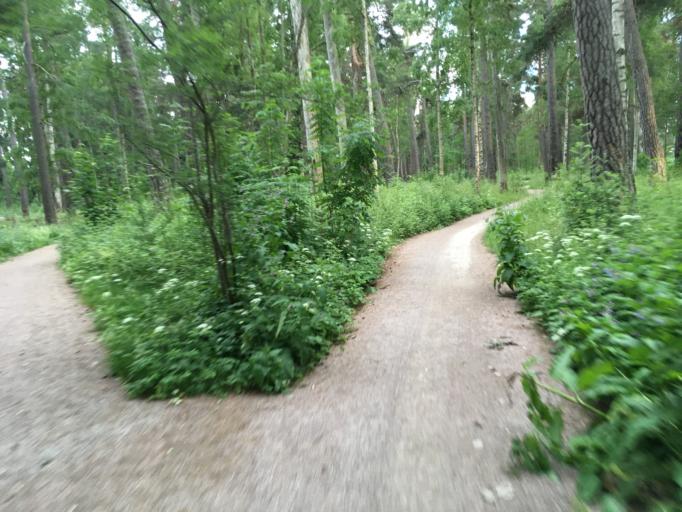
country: SE
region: Uppsala
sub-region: Uppsala Kommun
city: Uppsala
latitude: 59.8372
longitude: 17.6391
